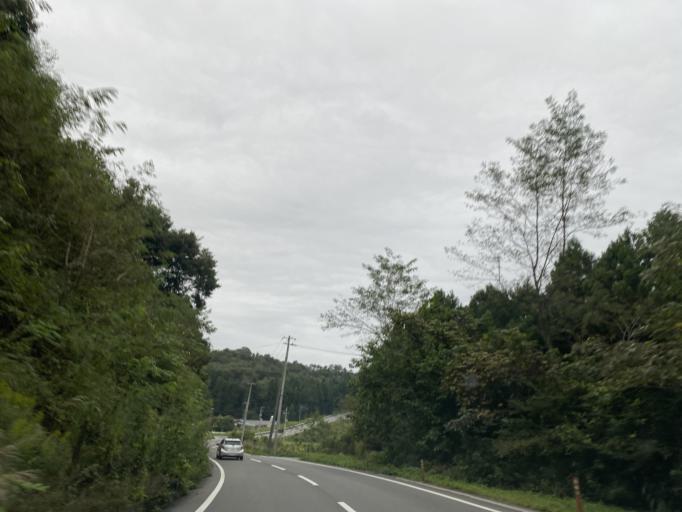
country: JP
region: Fukushima
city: Sukagawa
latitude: 37.2979
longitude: 140.2477
